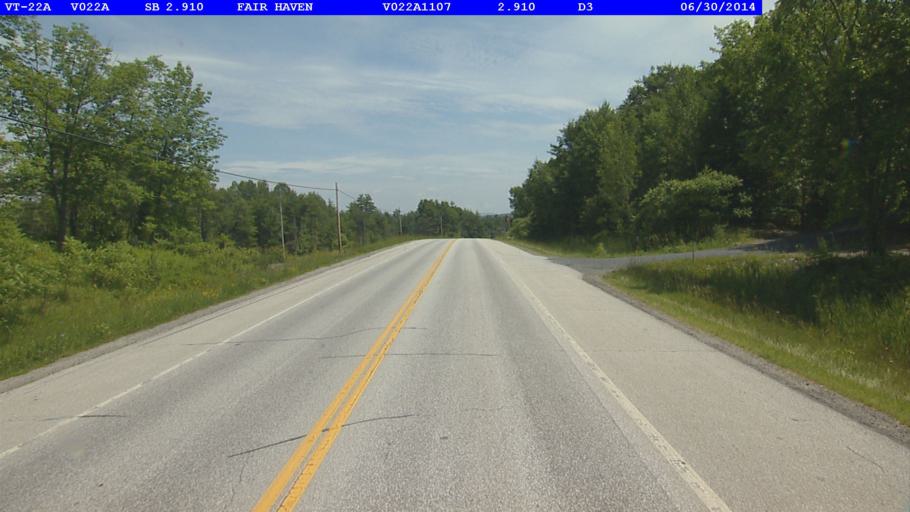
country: US
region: Vermont
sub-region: Rutland County
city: Fair Haven
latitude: 43.6104
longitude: -73.2834
